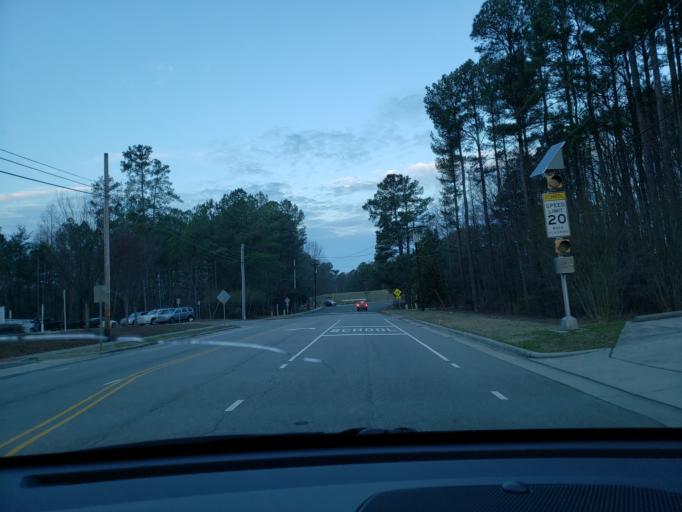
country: US
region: North Carolina
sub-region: Durham County
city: Durham
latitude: 35.9292
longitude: -78.9204
